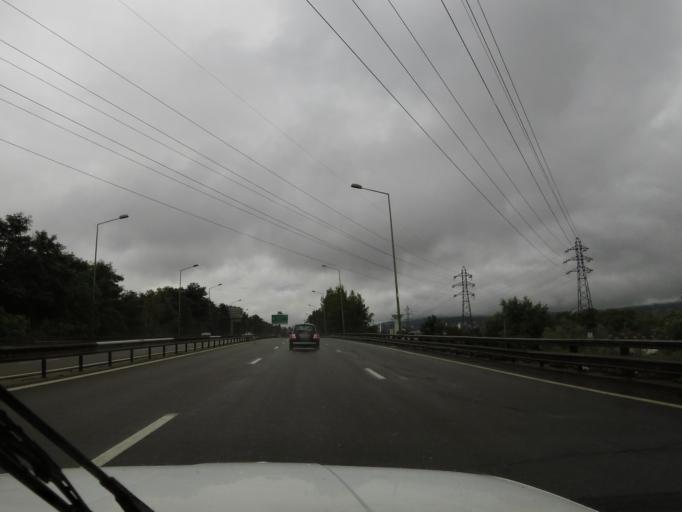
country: FR
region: Rhone-Alpes
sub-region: Departement de la Savoie
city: La Motte-Servolex
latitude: 45.5896
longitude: 5.9001
